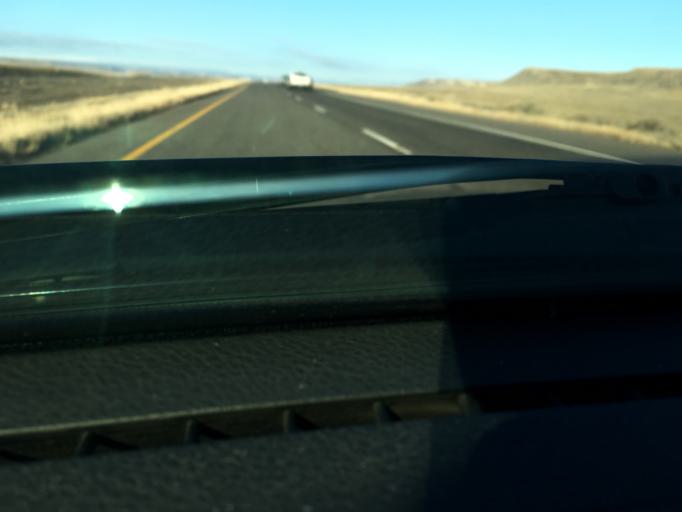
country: US
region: Colorado
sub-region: Delta County
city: Delta
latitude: 38.7554
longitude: -108.1739
